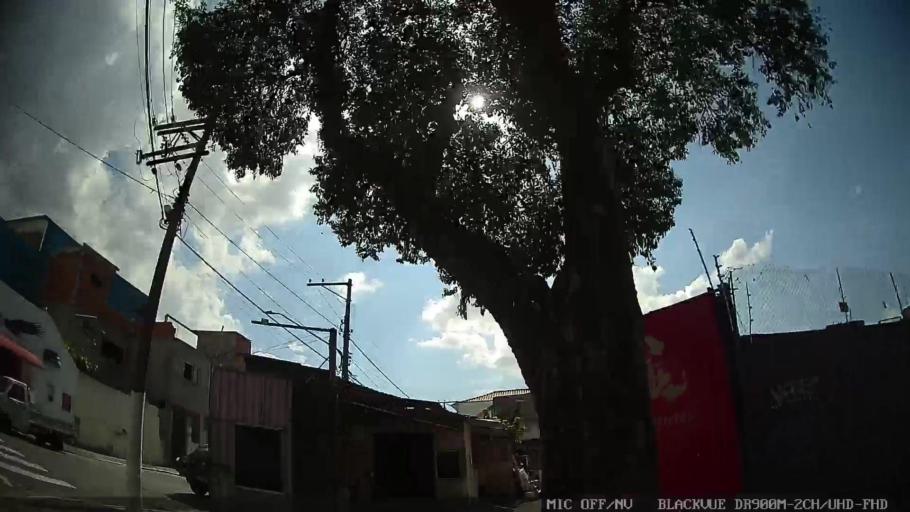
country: BR
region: Sao Paulo
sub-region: Ferraz De Vasconcelos
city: Ferraz de Vasconcelos
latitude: -23.5022
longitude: -46.4399
